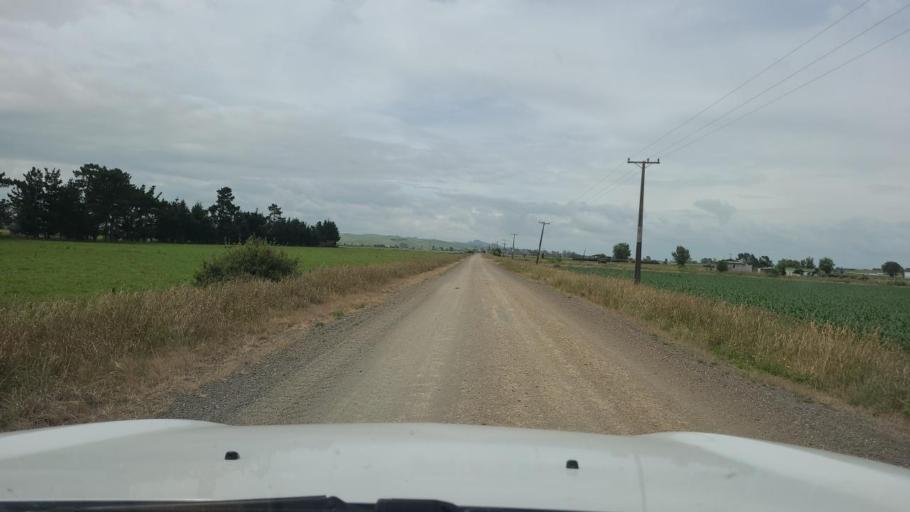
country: NZ
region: Waikato
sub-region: Hamilton City
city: Hamilton
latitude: -37.6658
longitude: 175.4385
